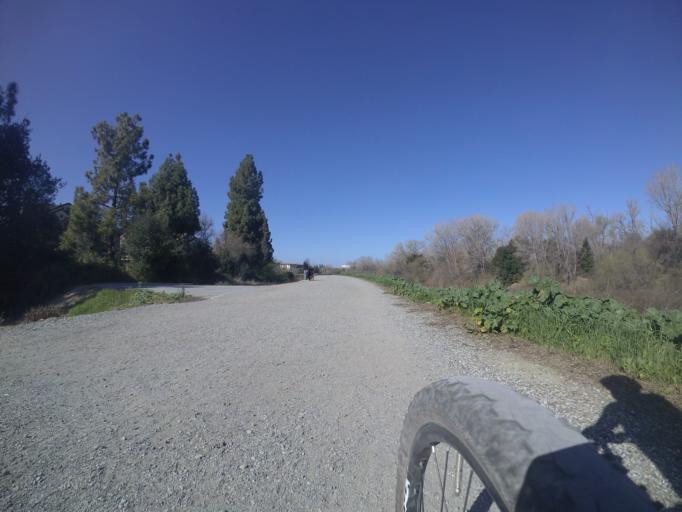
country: US
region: California
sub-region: Santa Clara County
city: Milpitas
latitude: 37.4035
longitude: -121.9198
